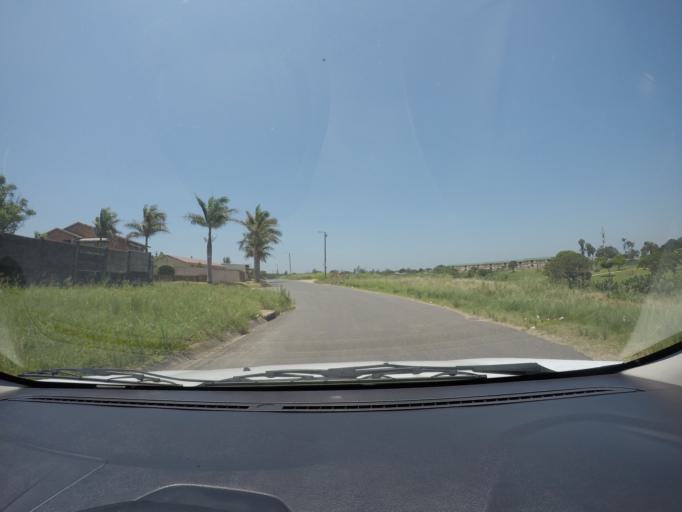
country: ZA
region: KwaZulu-Natal
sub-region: uThungulu District Municipality
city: eSikhawini
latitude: -28.8783
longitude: 31.9046
